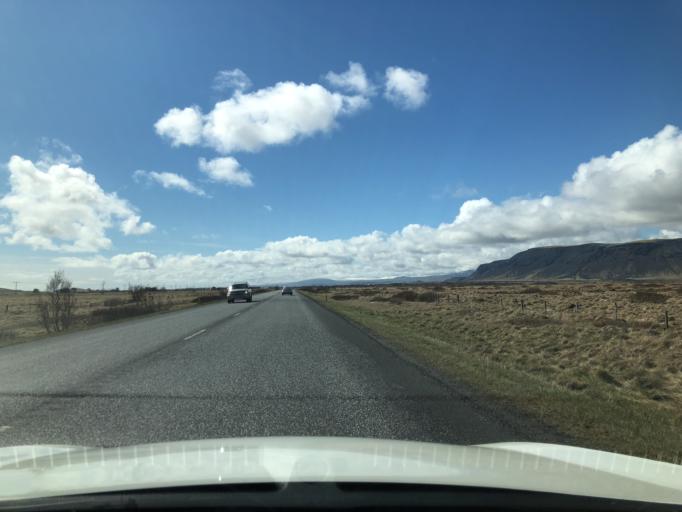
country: IS
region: South
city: Selfoss
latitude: 63.9423
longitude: -20.9029
